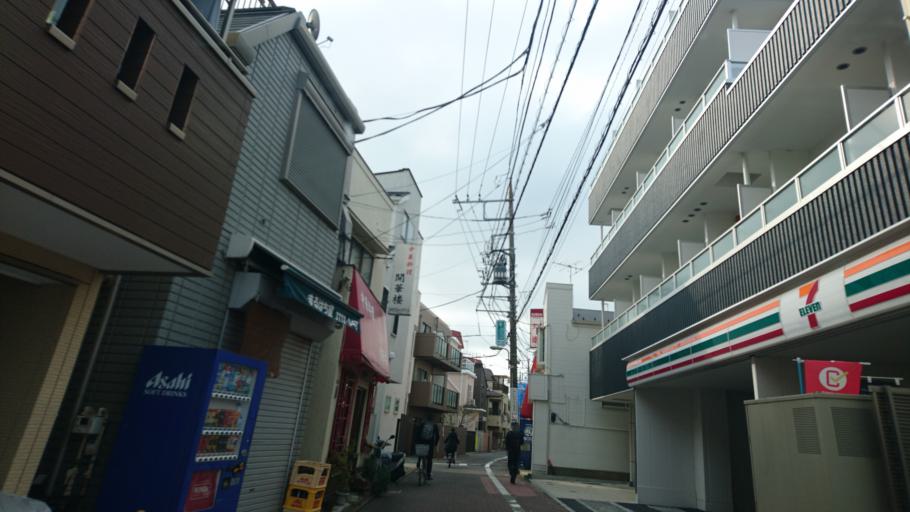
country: JP
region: Kanagawa
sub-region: Kawasaki-shi
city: Kawasaki
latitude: 35.5933
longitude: 139.7254
